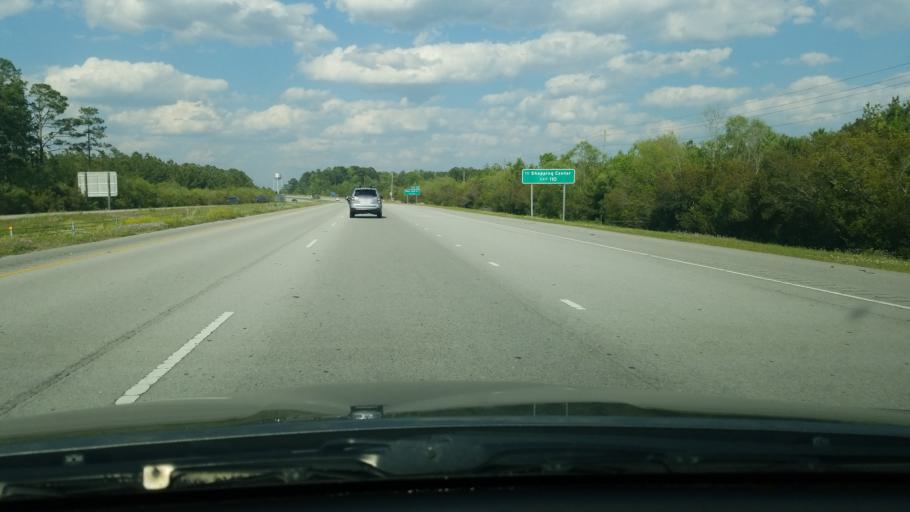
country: US
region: North Carolina
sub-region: Onslow County
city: Jacksonville
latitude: 34.7509
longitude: -77.4017
